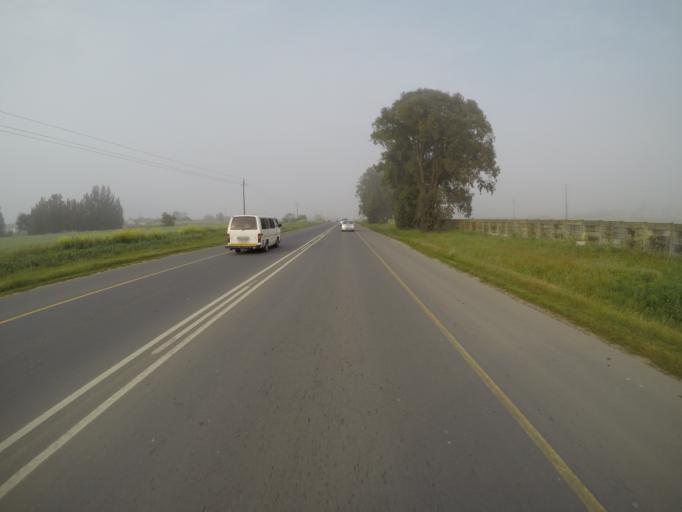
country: ZA
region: Western Cape
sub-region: City of Cape Town
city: Kraaifontein
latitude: -33.7867
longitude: 18.7016
